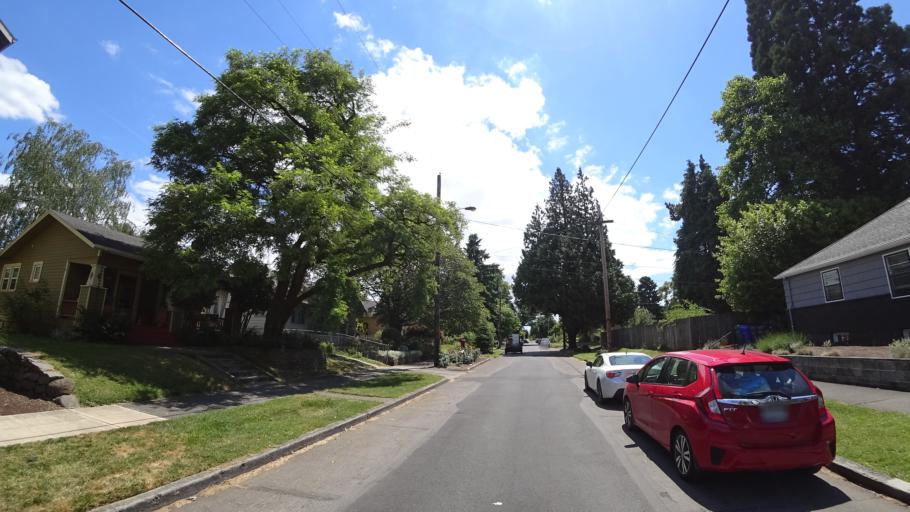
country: US
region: Oregon
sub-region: Multnomah County
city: Portland
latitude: 45.5646
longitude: -122.6802
